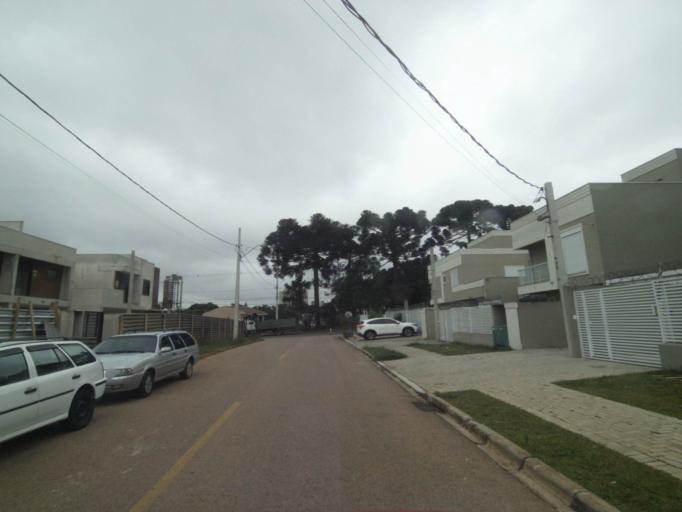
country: BR
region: Parana
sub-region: Curitiba
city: Curitiba
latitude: -25.4899
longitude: -49.3002
